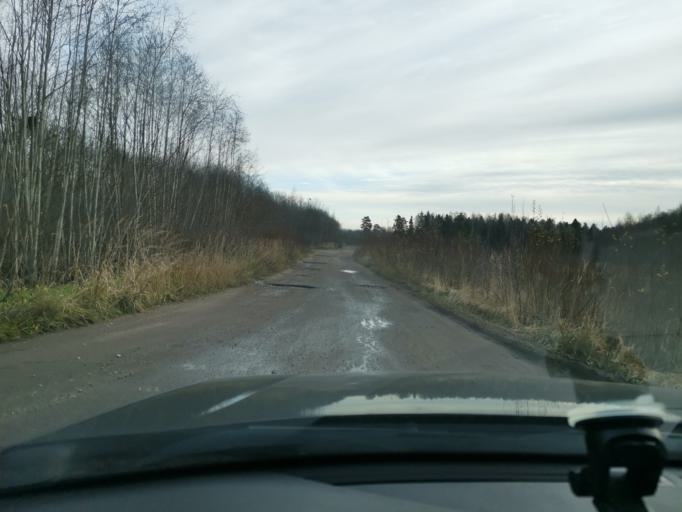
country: EE
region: Ida-Virumaa
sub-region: Sillamaee linn
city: Sillamae
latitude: 59.2598
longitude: 27.9108
